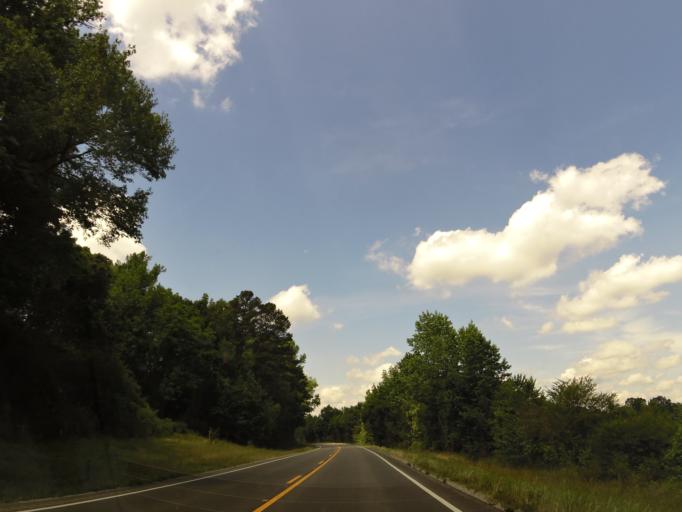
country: US
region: Alabama
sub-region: Marion County
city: Guin
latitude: 33.9510
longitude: -87.9774
